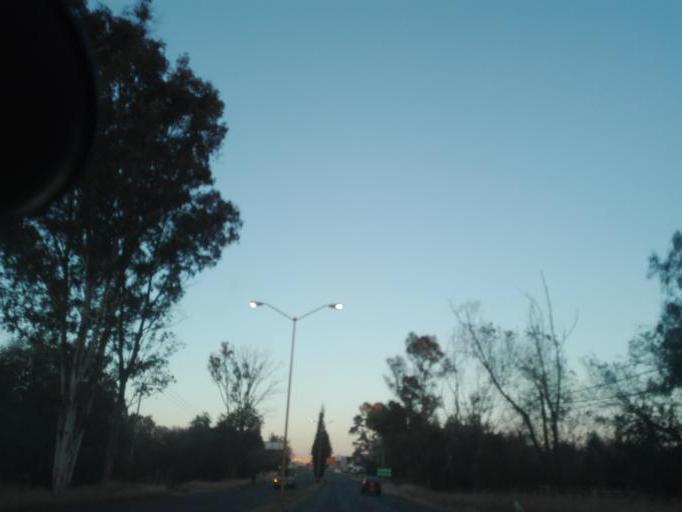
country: MX
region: Aguascalientes
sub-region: Aguascalientes
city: La Loma de los Negritos
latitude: 21.8653
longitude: -102.3321
